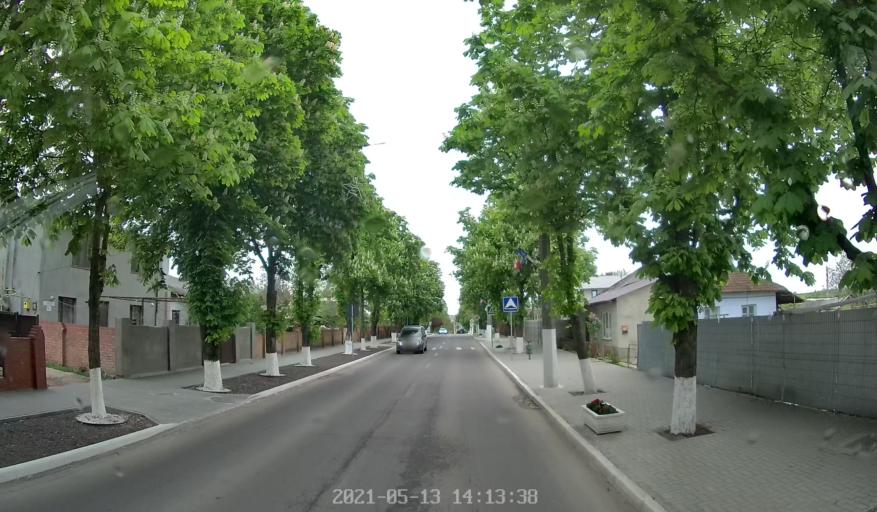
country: MD
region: Chisinau
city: Stauceni
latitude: 47.0898
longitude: 28.8683
